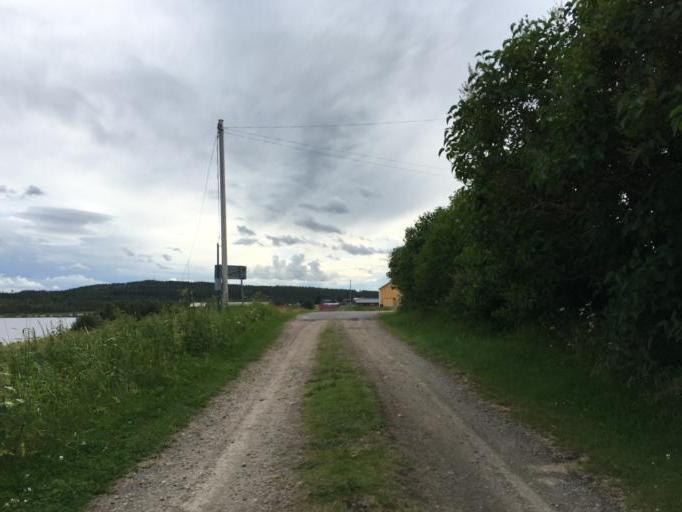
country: SE
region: Norrbotten
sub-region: Overkalix Kommun
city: OEverkalix
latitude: 66.1093
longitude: 22.7876
